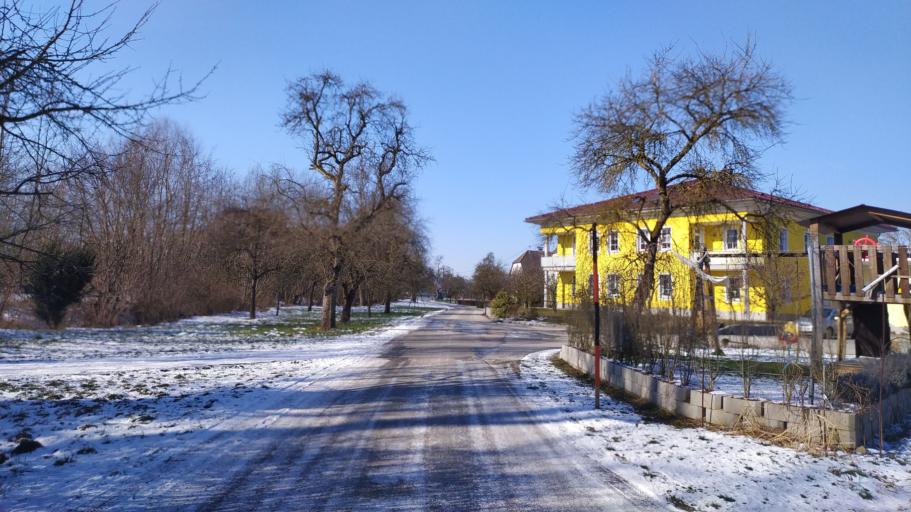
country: AT
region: Upper Austria
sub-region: Politischer Bezirk Urfahr-Umgebung
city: Goldworth
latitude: 48.3343
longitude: 14.0811
